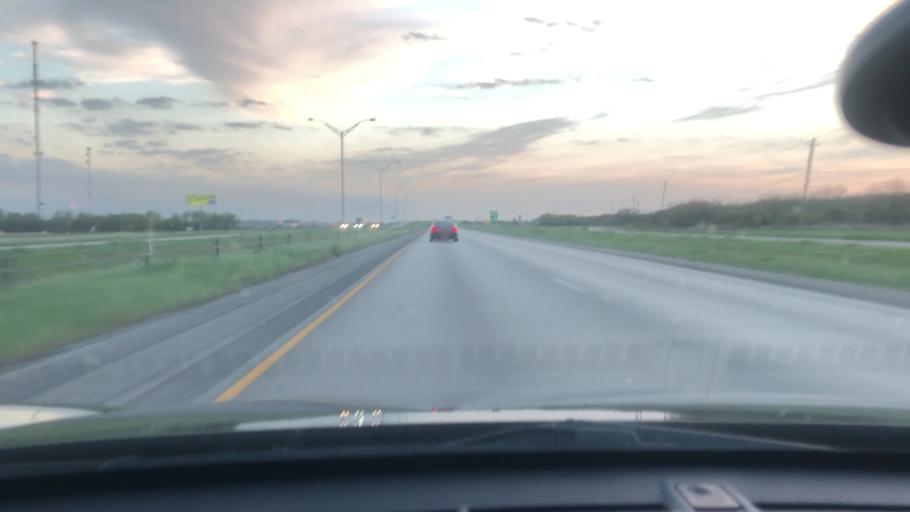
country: US
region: Texas
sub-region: Jackson County
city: Edna
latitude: 28.9762
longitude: -96.6662
